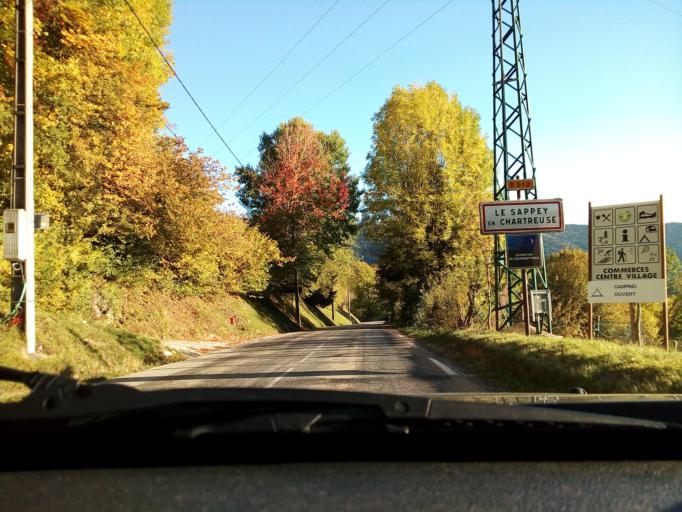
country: FR
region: Rhone-Alpes
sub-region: Departement de l'Isere
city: Le Sappey-en-Chartreuse
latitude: 45.2686
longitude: 5.7714
